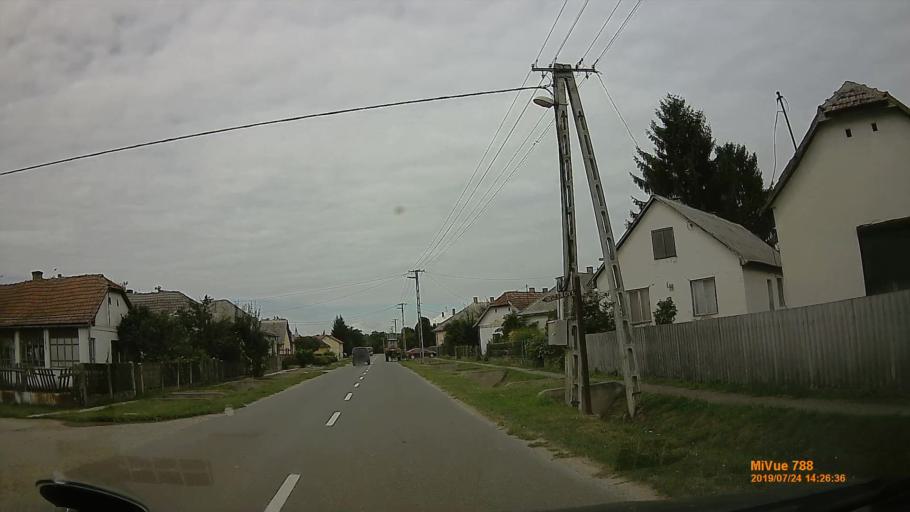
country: HU
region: Szabolcs-Szatmar-Bereg
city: Mandok
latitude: 48.3277
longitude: 22.2653
